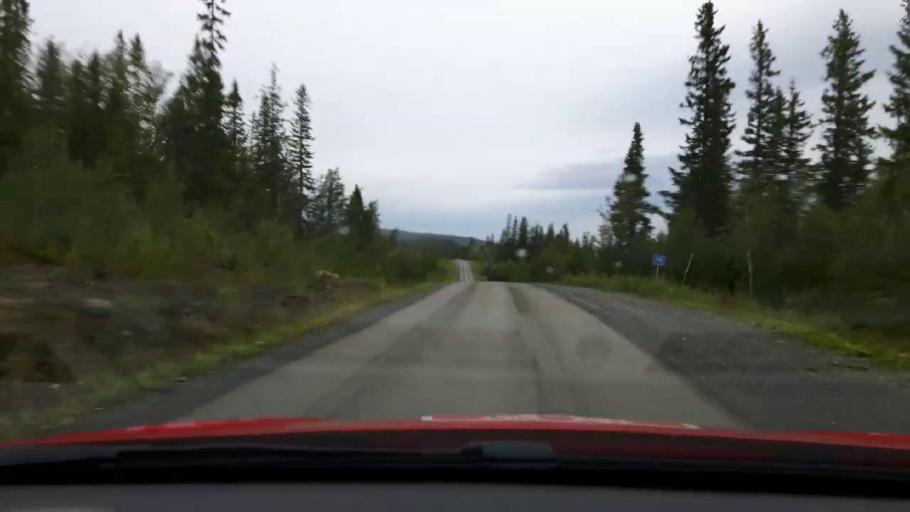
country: SE
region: Jaemtland
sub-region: Are Kommun
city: Are
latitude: 63.4155
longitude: 13.2298
